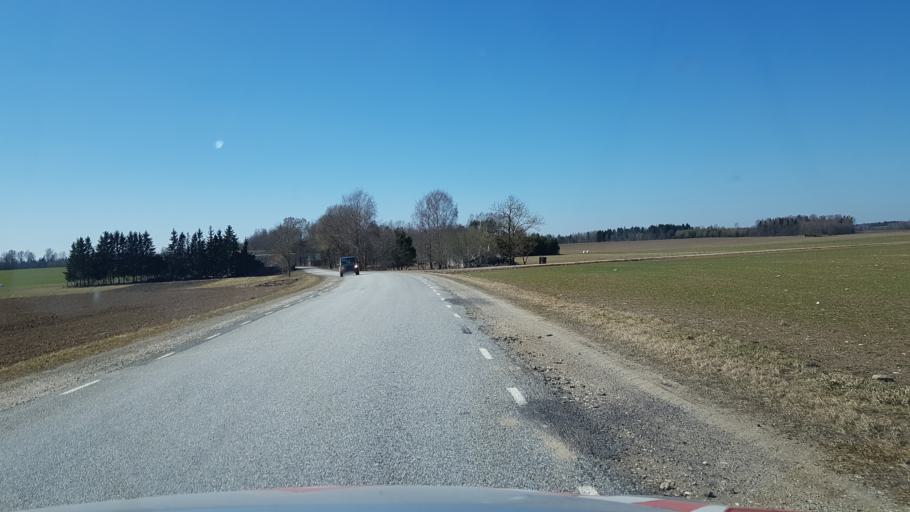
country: EE
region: Jaervamaa
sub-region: Koeru vald
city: Koeru
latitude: 59.0510
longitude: 26.0733
